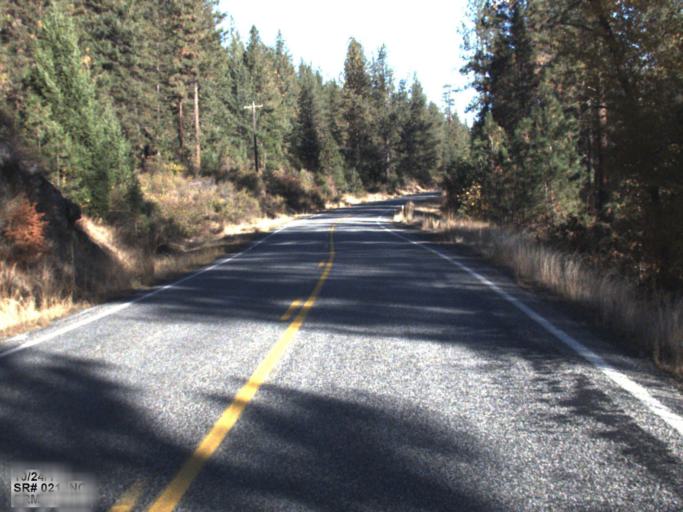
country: US
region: Washington
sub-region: Okanogan County
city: Coulee Dam
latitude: 48.0588
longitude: -118.6725
